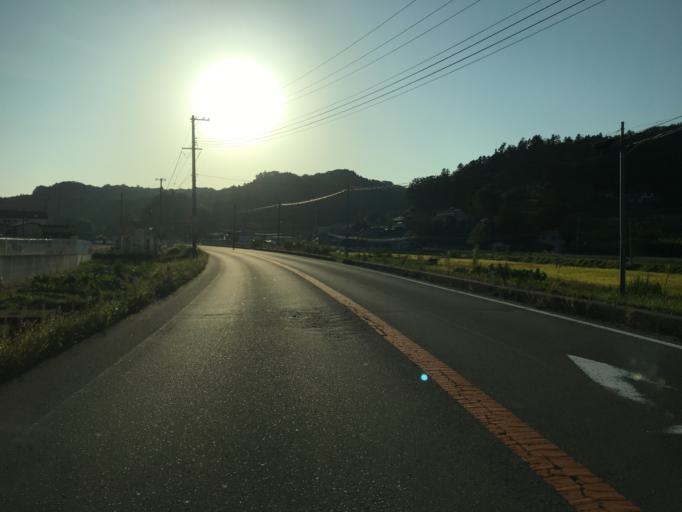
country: JP
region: Fukushima
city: Fukushima-shi
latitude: 37.6742
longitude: 140.5620
